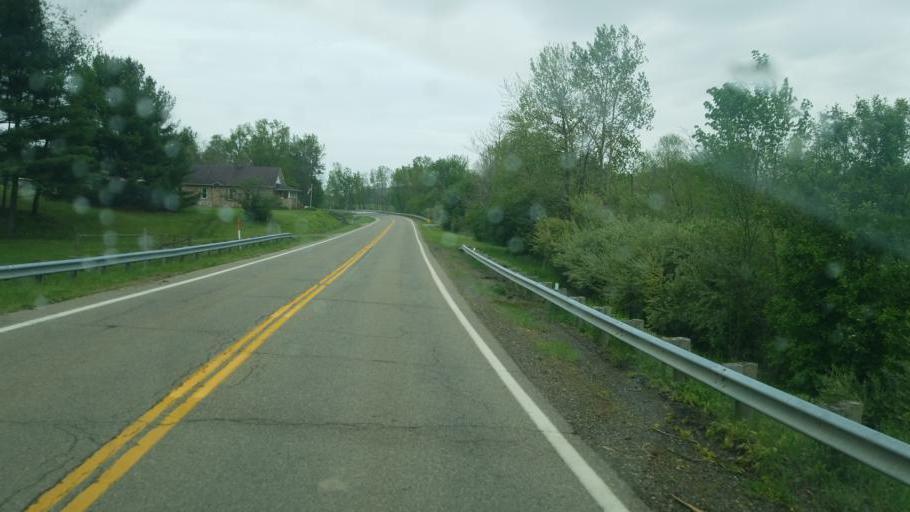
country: US
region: Ohio
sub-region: Coshocton County
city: West Lafayette
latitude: 40.2147
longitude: -81.7262
